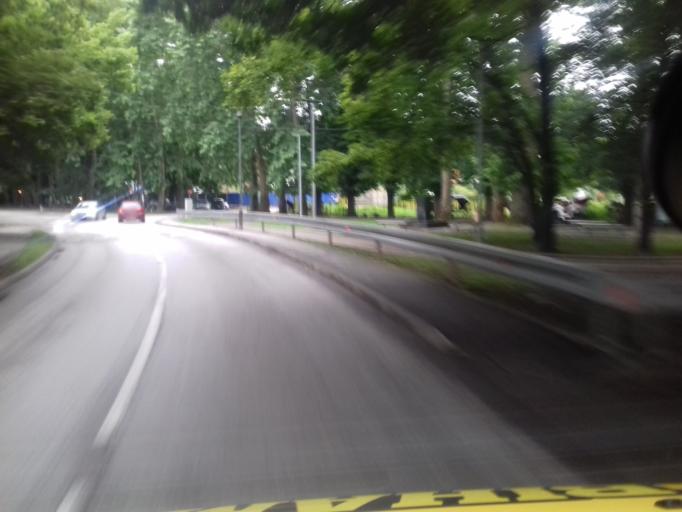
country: BA
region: Federation of Bosnia and Herzegovina
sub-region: Kanton Sarajevo
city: Sarajevo
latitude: 43.8246
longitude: 18.3023
